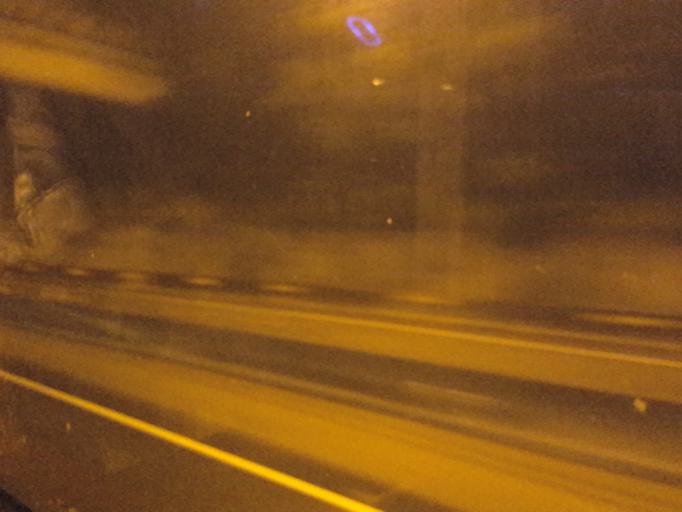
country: TW
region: Taiwan
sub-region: Hsinchu
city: Zhubei
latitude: 24.8579
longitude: 121.0106
